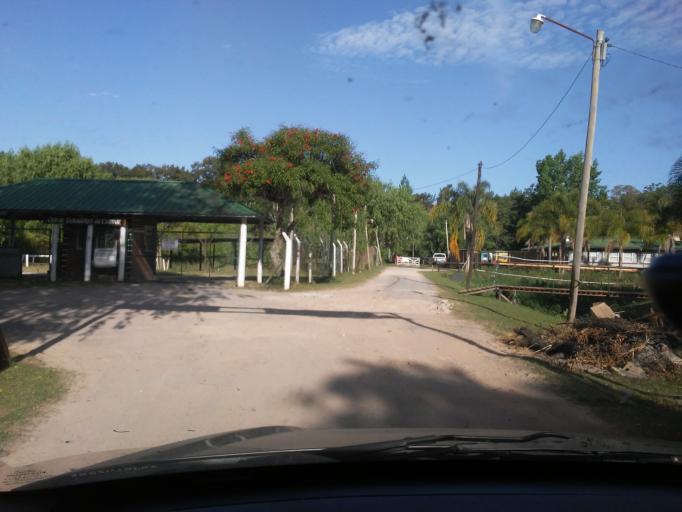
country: AR
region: Buenos Aires
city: Belen de Escobar
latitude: -34.2500
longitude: -58.7184
